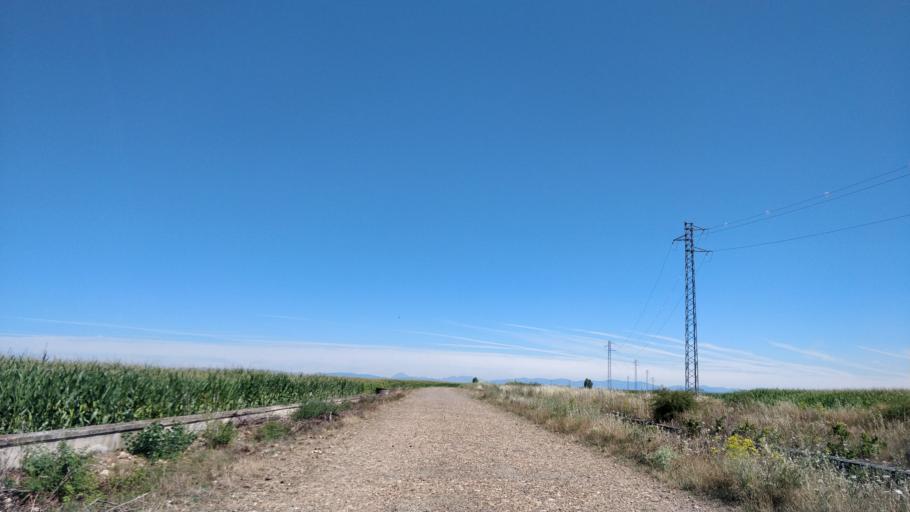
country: ES
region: Castille and Leon
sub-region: Provincia de Leon
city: Bustillo del Paramo
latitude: 42.4308
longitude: -5.8220
